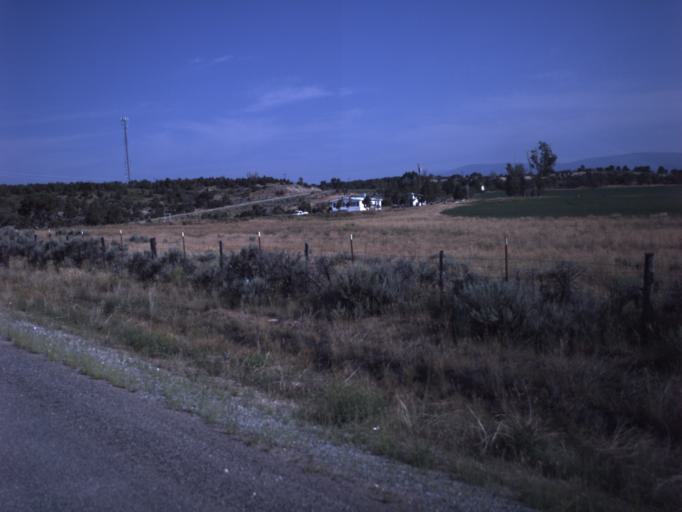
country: US
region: Utah
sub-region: Duchesne County
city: Duchesne
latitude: 40.3561
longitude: -110.3853
